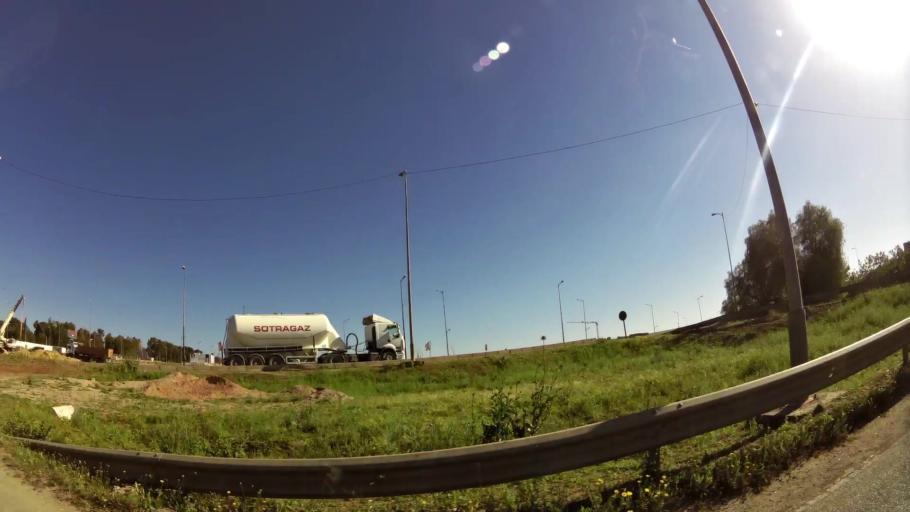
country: MA
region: Fes-Boulemane
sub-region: Fes
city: Fes
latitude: 33.9912
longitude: -5.0222
